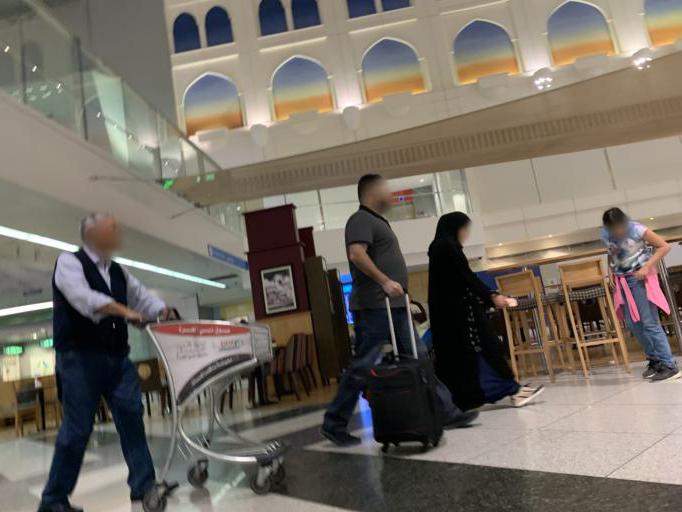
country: AE
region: Ash Shariqah
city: Sharjah
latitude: 25.2532
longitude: 55.3531
